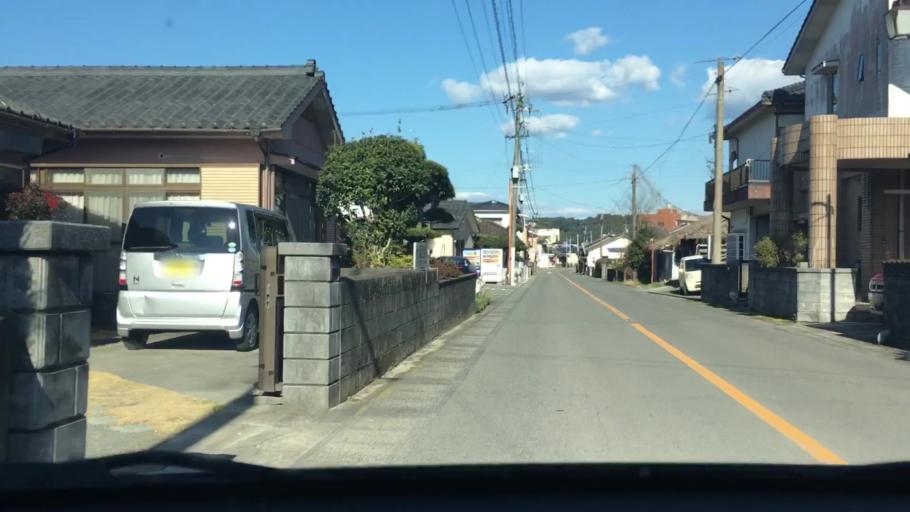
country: JP
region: Kagoshima
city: Satsumasendai
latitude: 31.7862
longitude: 130.4030
